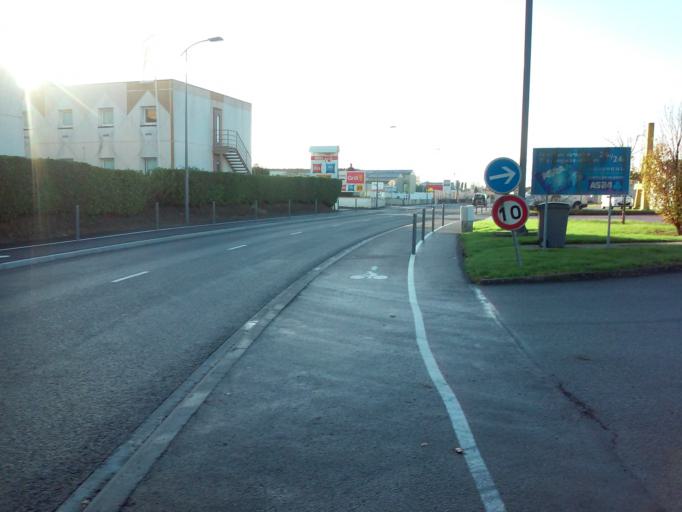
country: FR
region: Pays de la Loire
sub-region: Departement de la Vendee
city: Mouilleron-le-Captif
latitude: 46.7105
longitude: -1.4309
